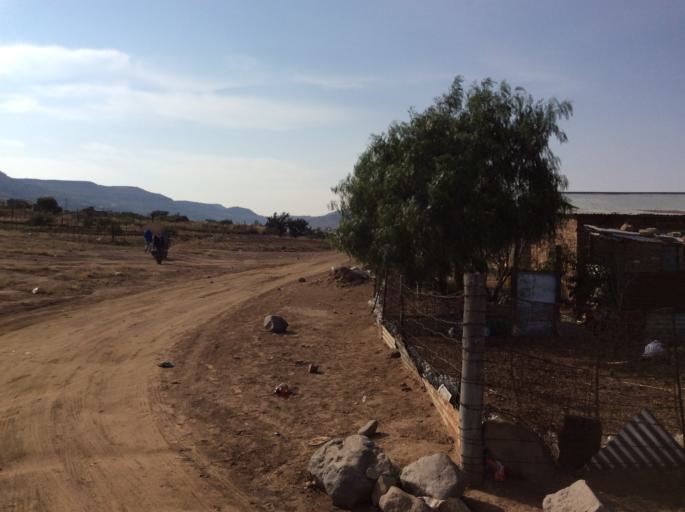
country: LS
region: Mafeteng
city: Mafeteng
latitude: -29.7176
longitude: 27.0110
